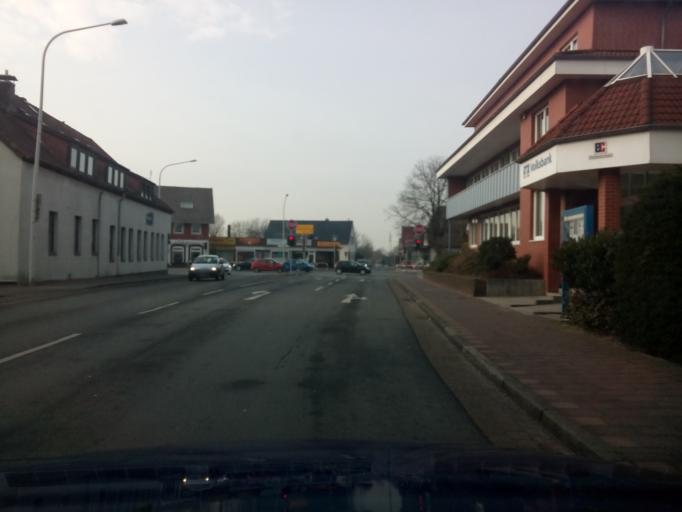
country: DE
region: Lower Saxony
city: Langen
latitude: 53.6082
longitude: 8.5951
